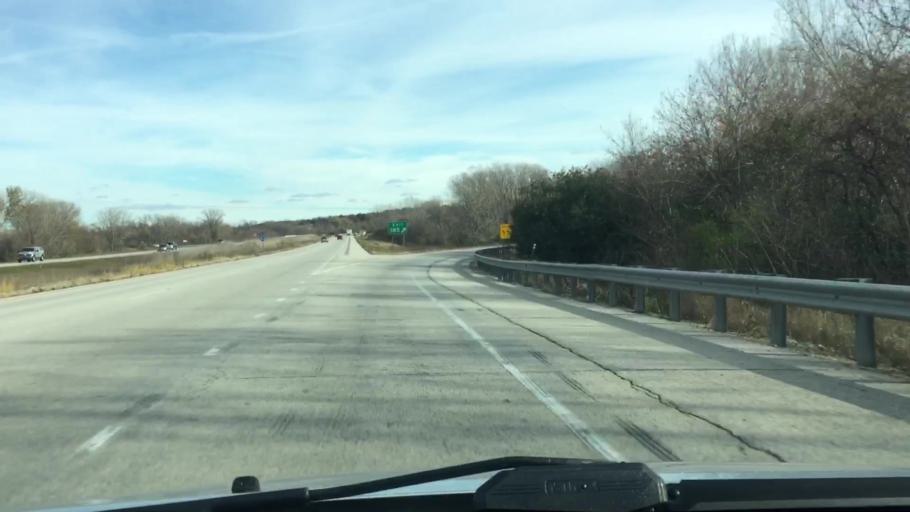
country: US
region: Wisconsin
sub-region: Brown County
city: Green Bay
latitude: 44.5195
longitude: -87.9640
